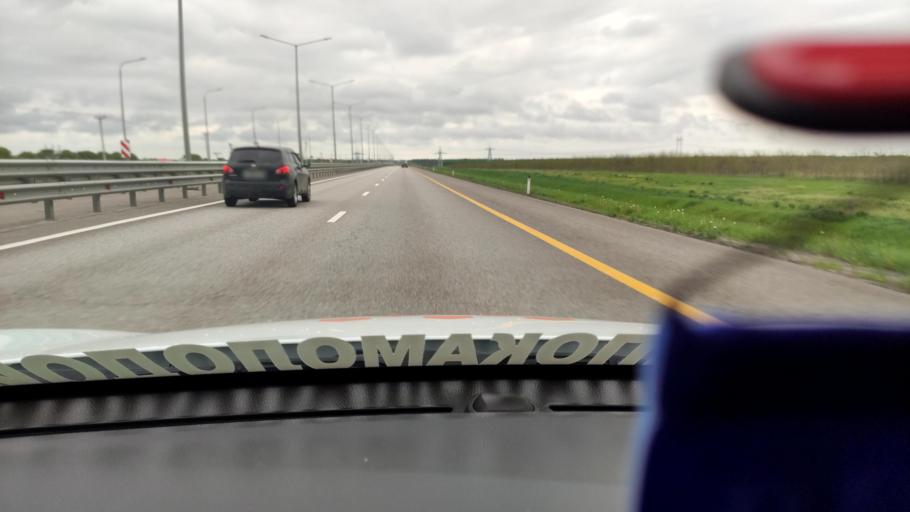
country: RU
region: Voronezj
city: Podkletnoye
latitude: 51.5580
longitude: 39.4844
